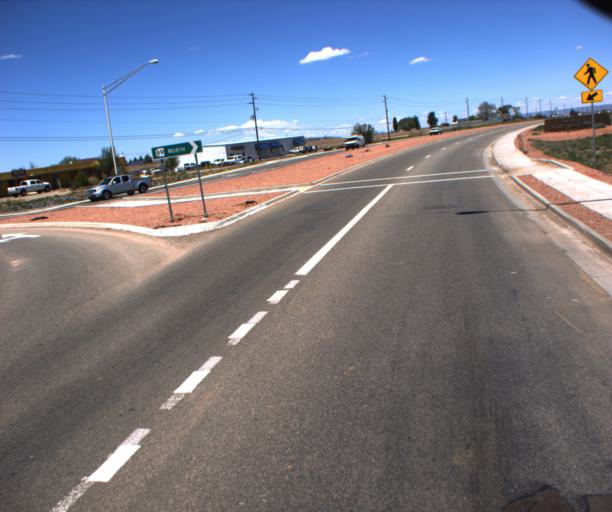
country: US
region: Arizona
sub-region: Yavapai County
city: Chino Valley
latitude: 34.7167
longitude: -112.4531
